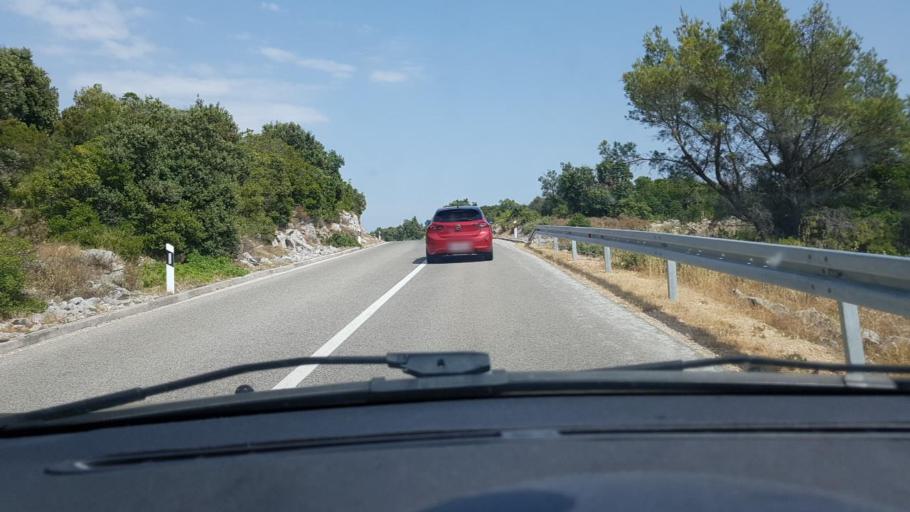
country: HR
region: Dubrovacko-Neretvanska
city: Smokvica
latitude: 42.9486
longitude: 16.9780
